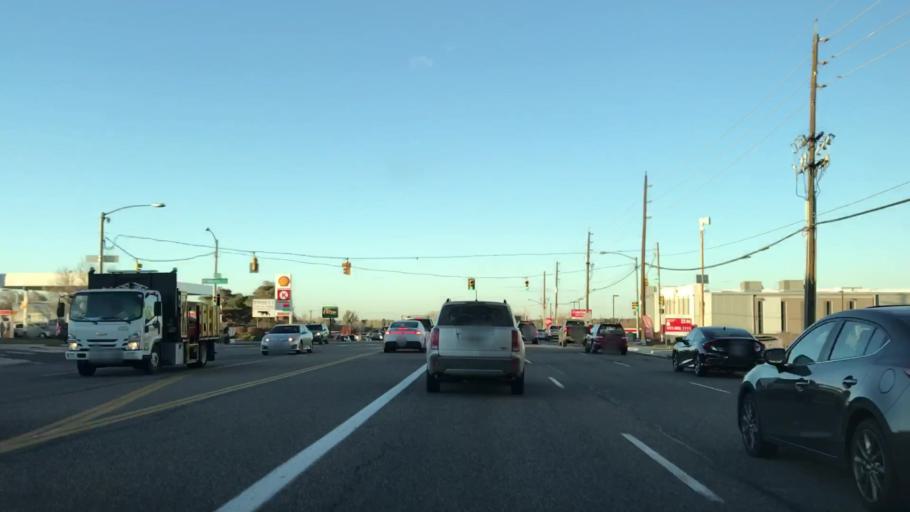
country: US
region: Colorado
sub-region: Arapahoe County
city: Castlewood
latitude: 39.6506
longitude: -104.8848
